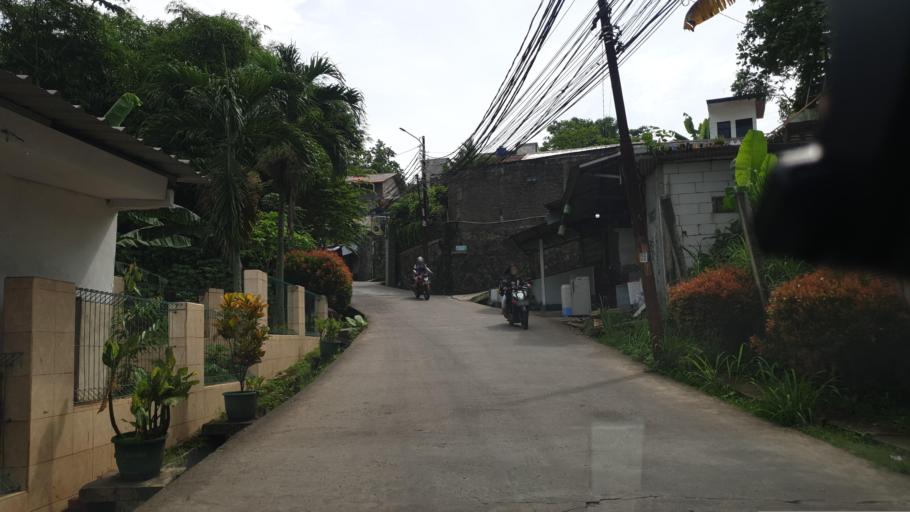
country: ID
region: West Java
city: Pamulang
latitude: -6.3471
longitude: 106.7750
